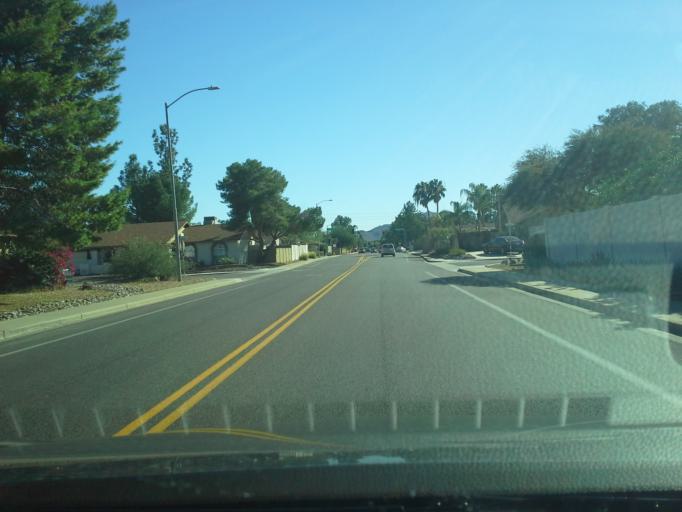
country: US
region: Arizona
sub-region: Maricopa County
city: Paradise Valley
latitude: 33.6134
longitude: -111.9866
